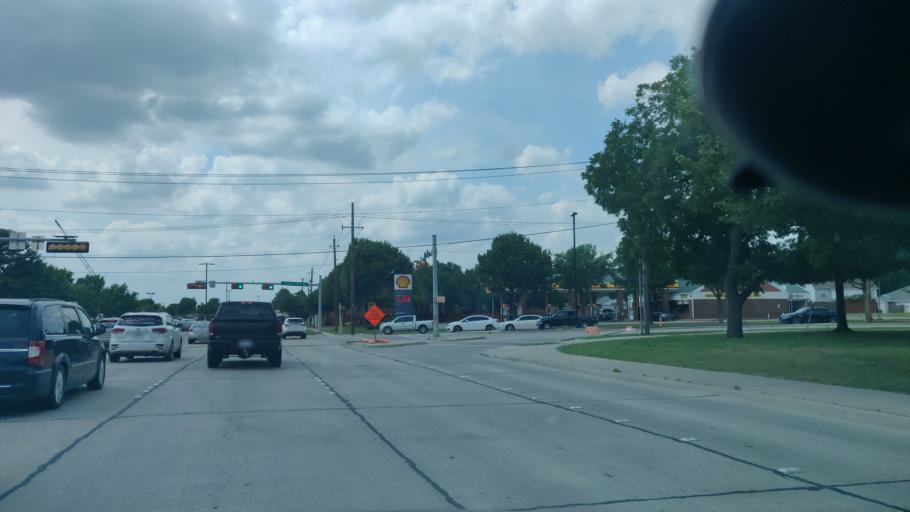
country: US
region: Texas
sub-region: Dallas County
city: Sachse
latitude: 32.9372
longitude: -96.6026
